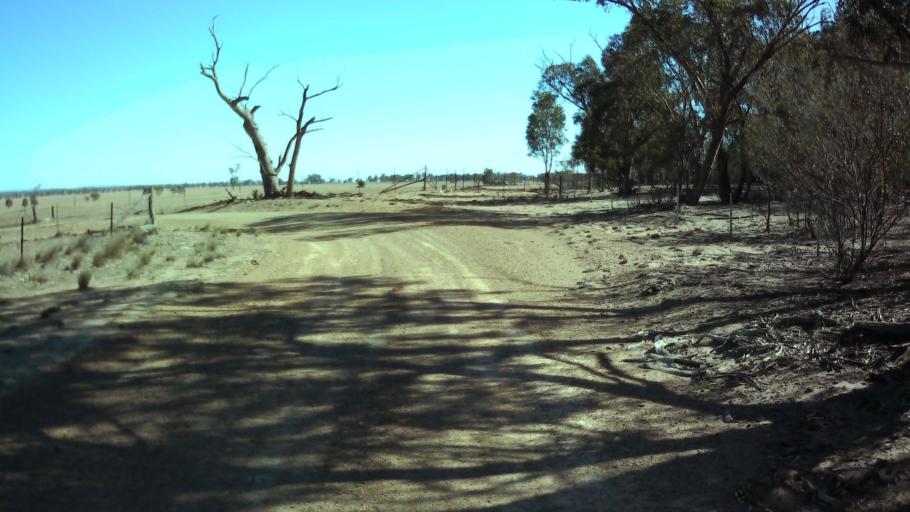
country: AU
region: New South Wales
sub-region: Weddin
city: Grenfell
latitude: -33.7541
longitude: 147.9202
